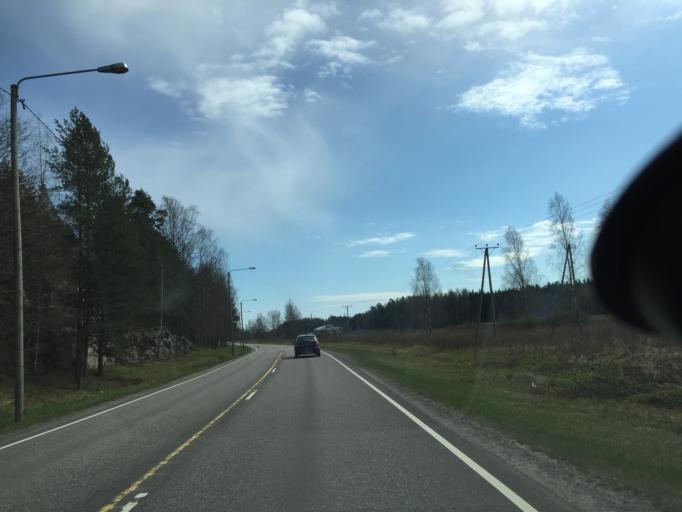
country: FI
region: Uusimaa
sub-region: Raaseporin
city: Ekenaes
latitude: 60.0012
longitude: 23.4028
